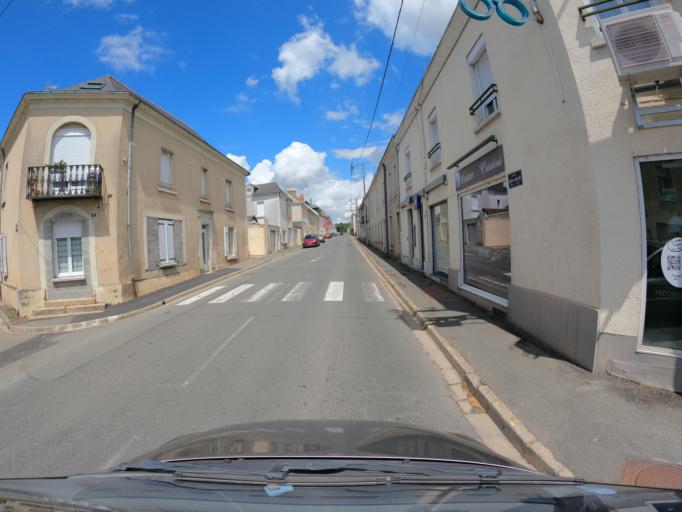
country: FR
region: Pays de la Loire
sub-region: Departement de Maine-et-Loire
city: Champigne
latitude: 47.6642
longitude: -0.5718
